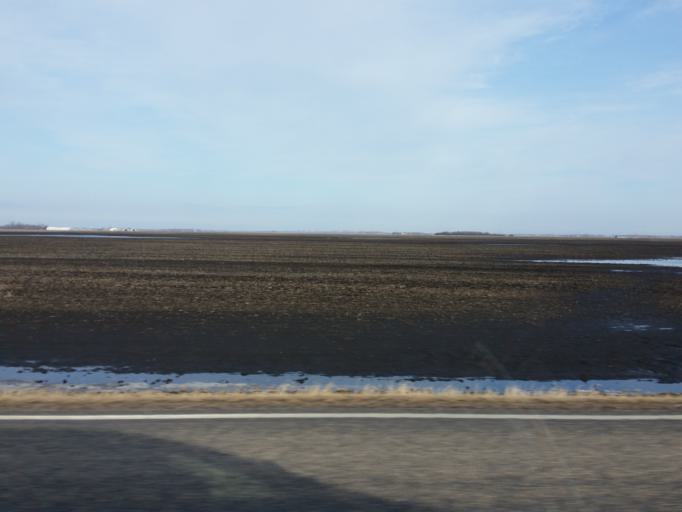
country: US
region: North Dakota
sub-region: Walsh County
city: Grafton
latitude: 48.4173
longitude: -97.2996
